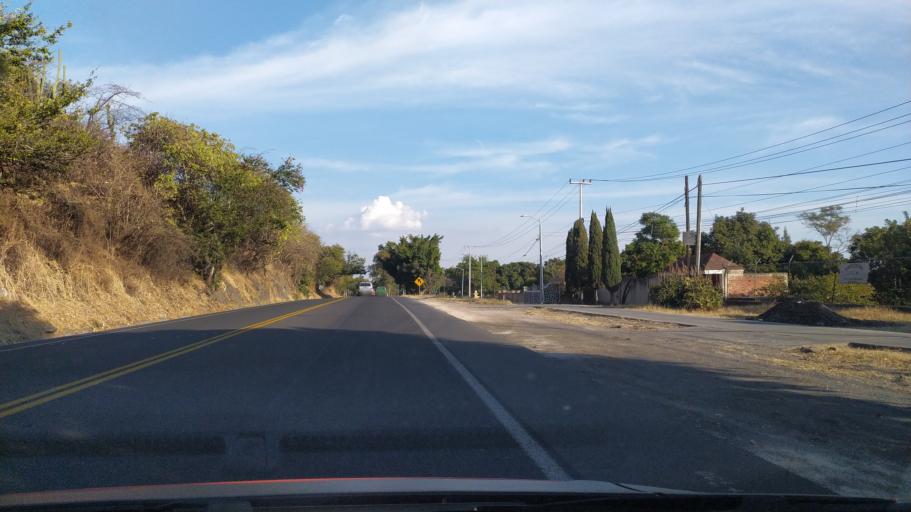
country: MX
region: Jalisco
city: Jamay
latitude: 20.2936
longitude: -102.7316
